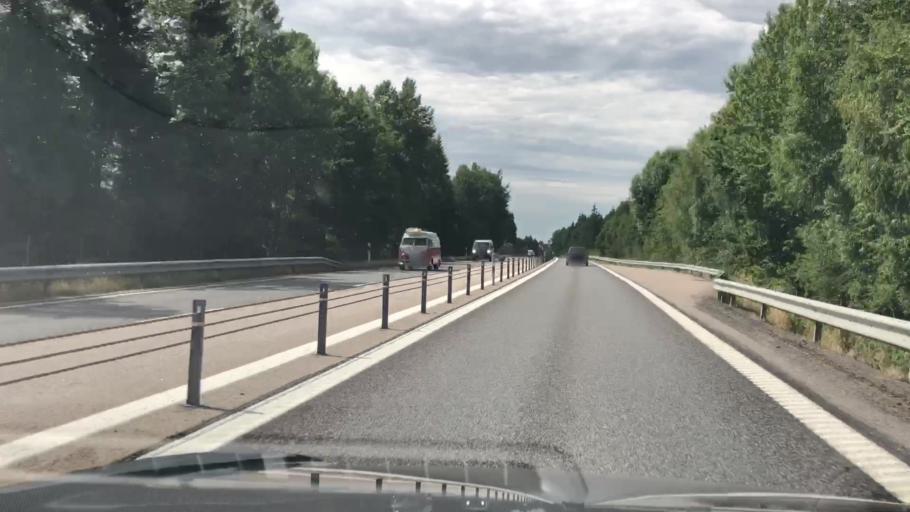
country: SE
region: Blekinge
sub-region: Ronneby Kommun
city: Ronneby
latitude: 56.2267
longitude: 15.2271
